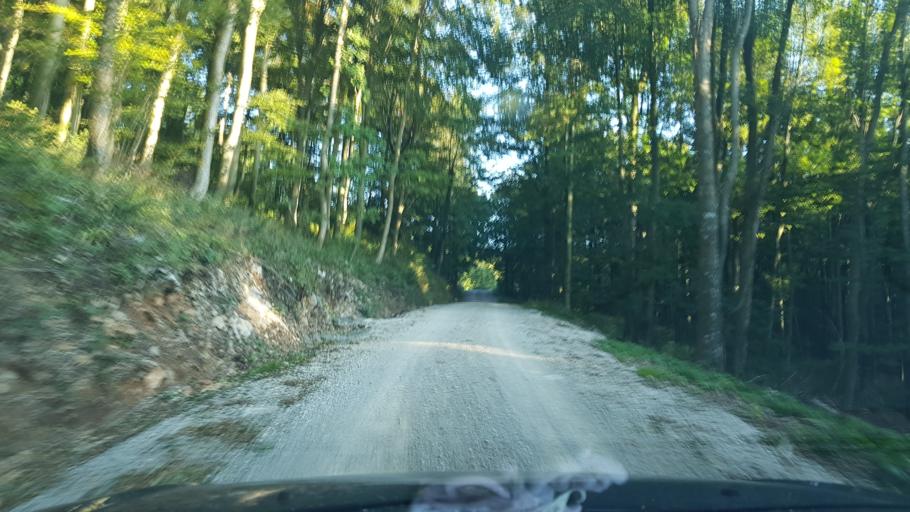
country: SI
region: Vipava
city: Vipava
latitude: 45.7806
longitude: 14.0431
